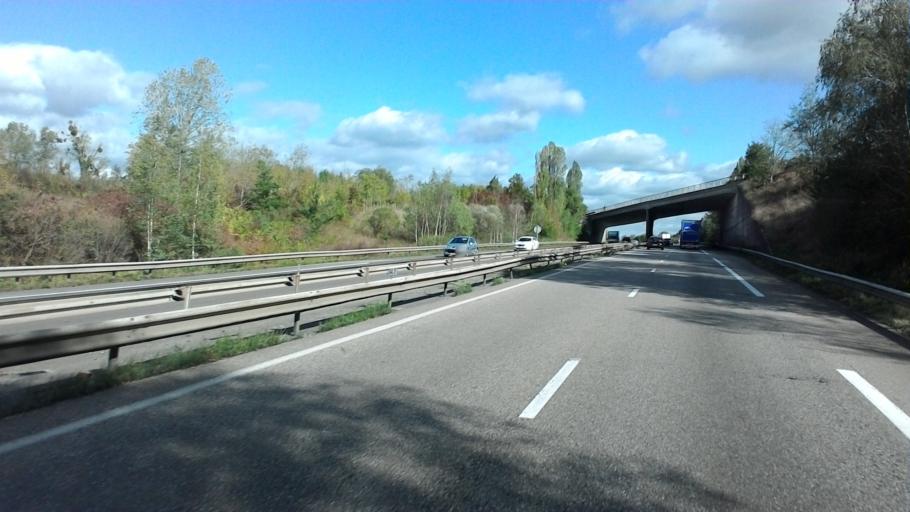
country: FR
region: Lorraine
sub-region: Departement de Meurthe-et-Moselle
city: Dommartin-les-Toul
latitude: 48.6800
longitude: 5.9350
